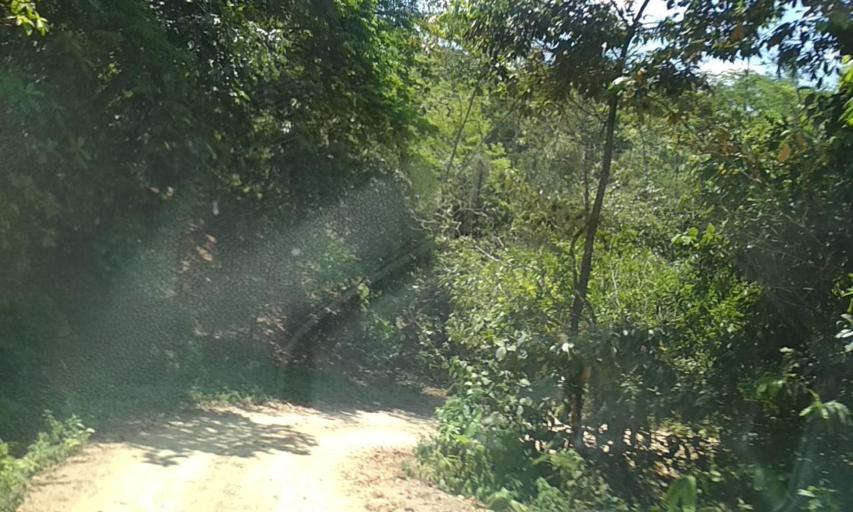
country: MX
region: Chiapas
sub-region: Tecpatan
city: Raudales Malpaso
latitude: 17.3942
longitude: -93.7266
